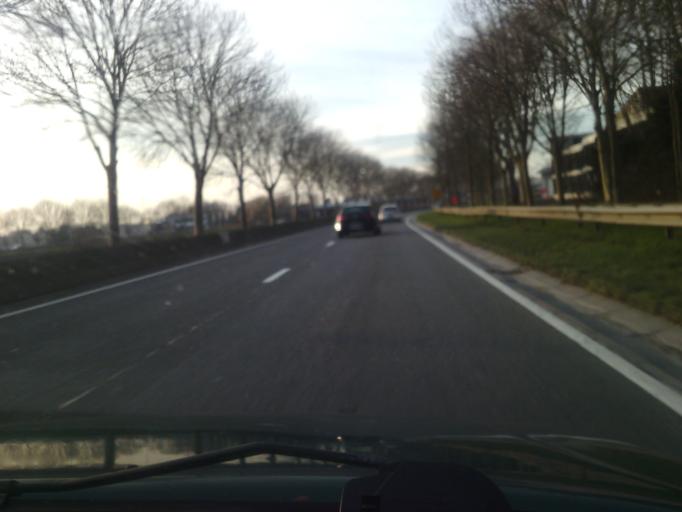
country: BE
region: Flanders
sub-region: Provincie Oost-Vlaanderen
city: Gent
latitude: 51.0333
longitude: 3.6922
